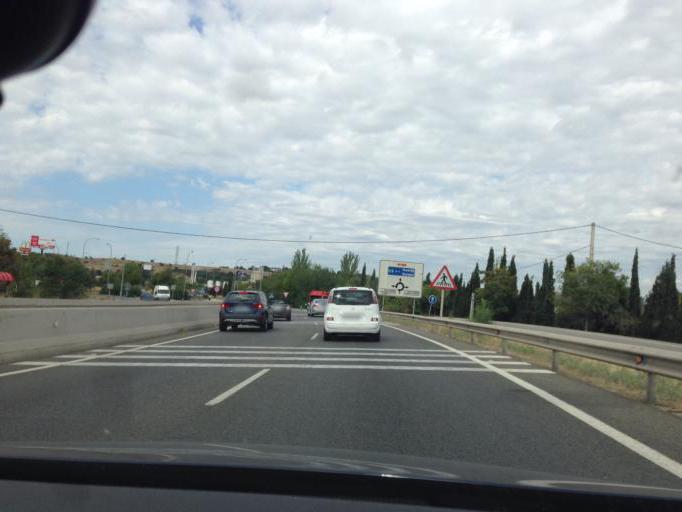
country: ES
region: Madrid
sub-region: Provincia de Madrid
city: San Sebastian de los Reyes
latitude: 40.5835
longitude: -3.5732
